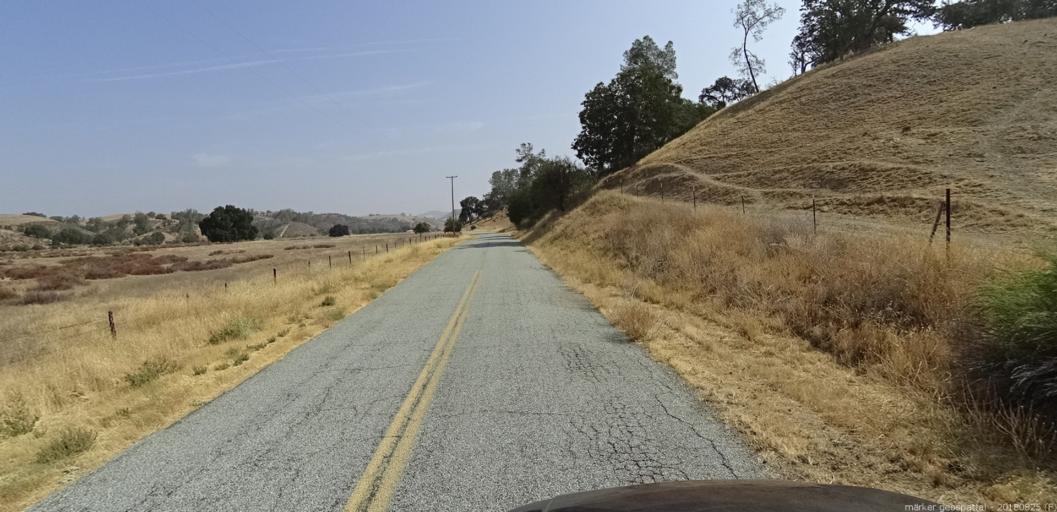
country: US
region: California
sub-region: San Luis Obispo County
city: San Miguel
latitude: 35.8420
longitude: -120.6171
